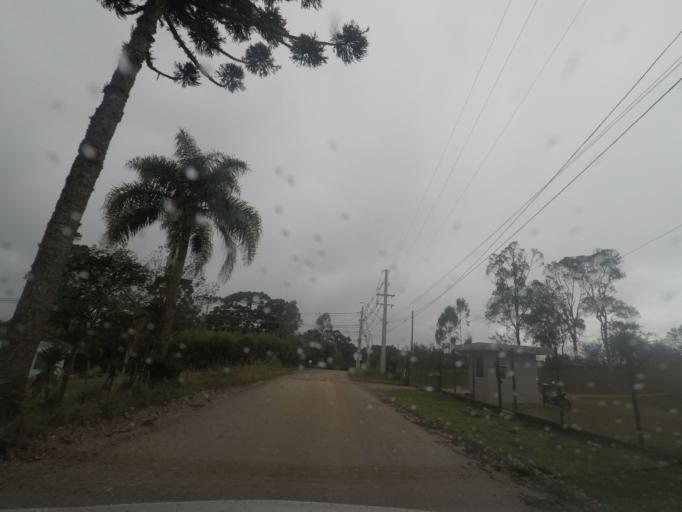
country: BR
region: Parana
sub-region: Campina Grande Do Sul
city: Campina Grande do Sul
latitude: -25.3130
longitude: -49.0794
